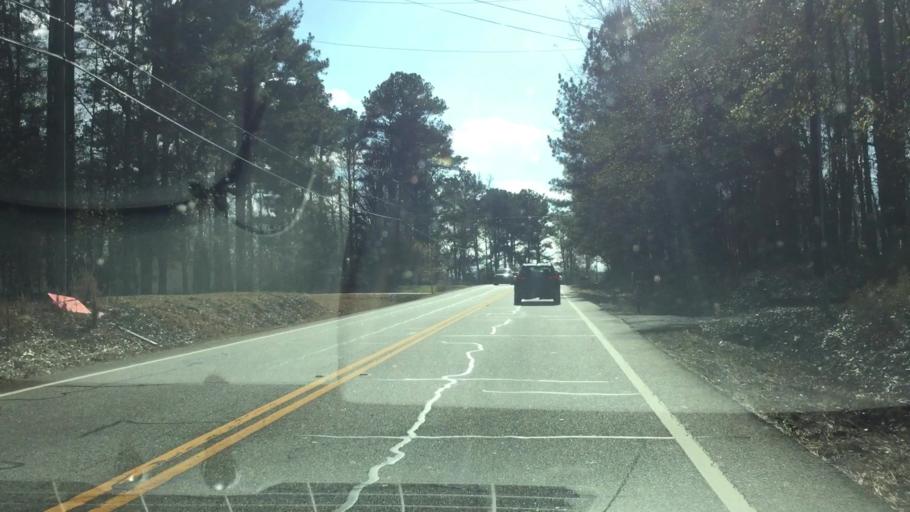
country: US
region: Georgia
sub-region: Henry County
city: McDonough
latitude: 33.4710
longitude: -84.1395
